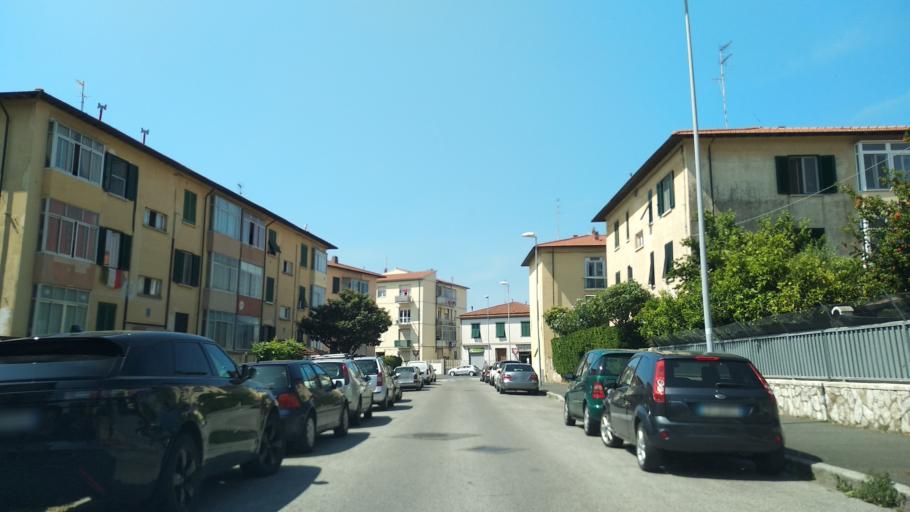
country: IT
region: Tuscany
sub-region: Provincia di Livorno
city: Livorno
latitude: 43.5637
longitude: 10.3316
